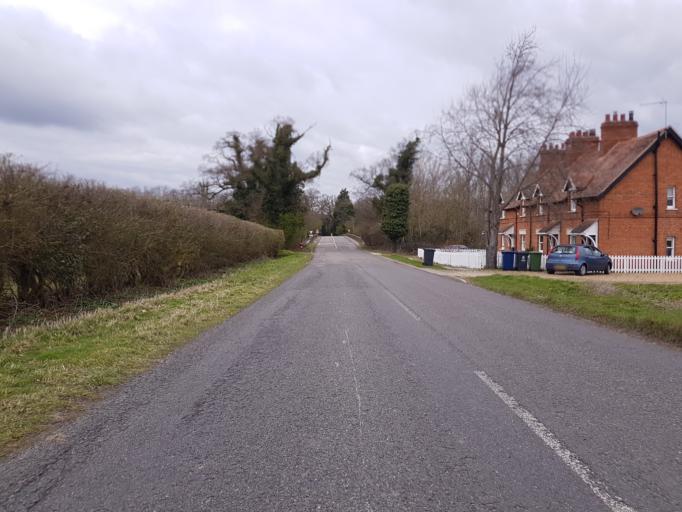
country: GB
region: England
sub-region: Cambridgeshire
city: Girton
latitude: 52.2208
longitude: 0.0498
